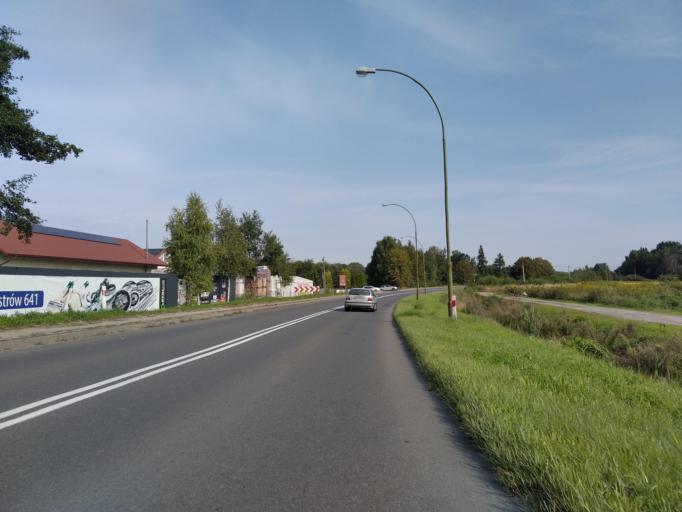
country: PL
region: Subcarpathian Voivodeship
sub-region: Powiat ropczycko-sedziszowski
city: Ostrow
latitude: 50.0811
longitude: 21.5835
